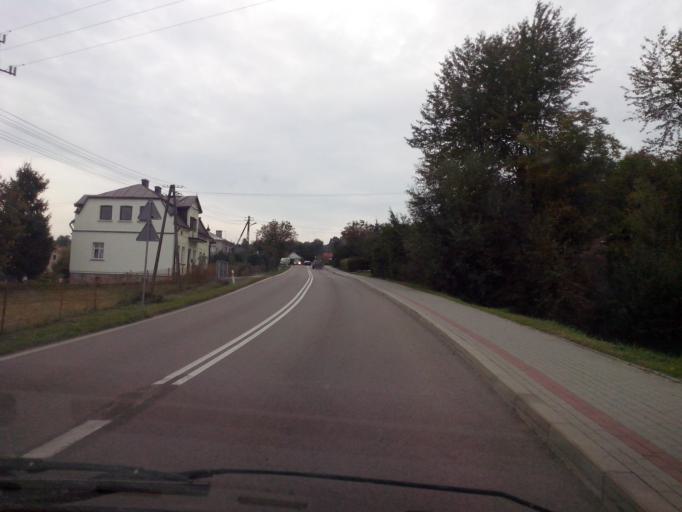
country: PL
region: Subcarpathian Voivodeship
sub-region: Powiat jaroslawski
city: Kramarzowka
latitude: 49.8199
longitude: 22.4756
